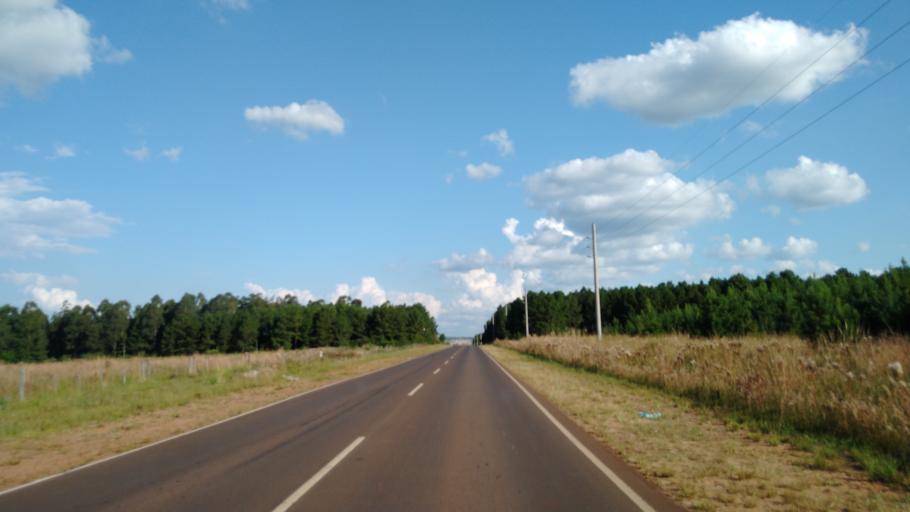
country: PY
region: Itapua
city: San Juan del Parana
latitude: -27.3802
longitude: -55.9918
